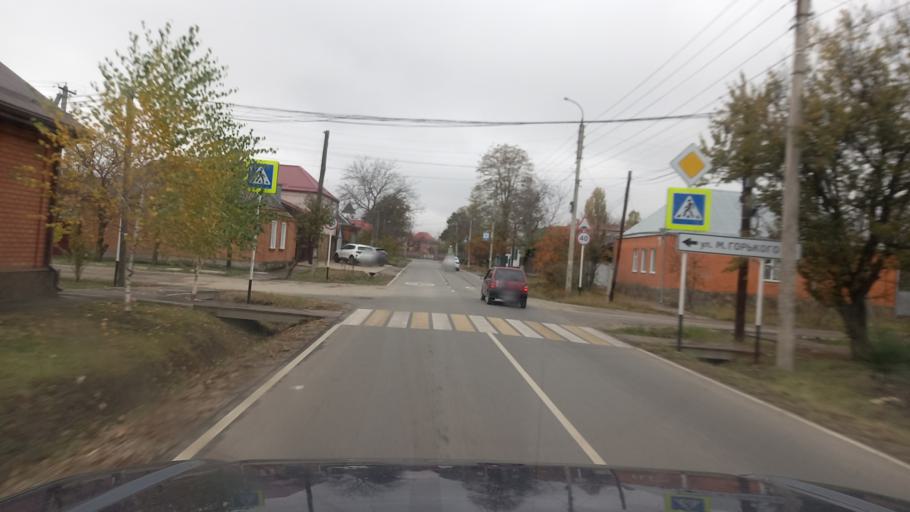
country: RU
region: Adygeya
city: Maykop
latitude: 44.6007
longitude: 40.0750
